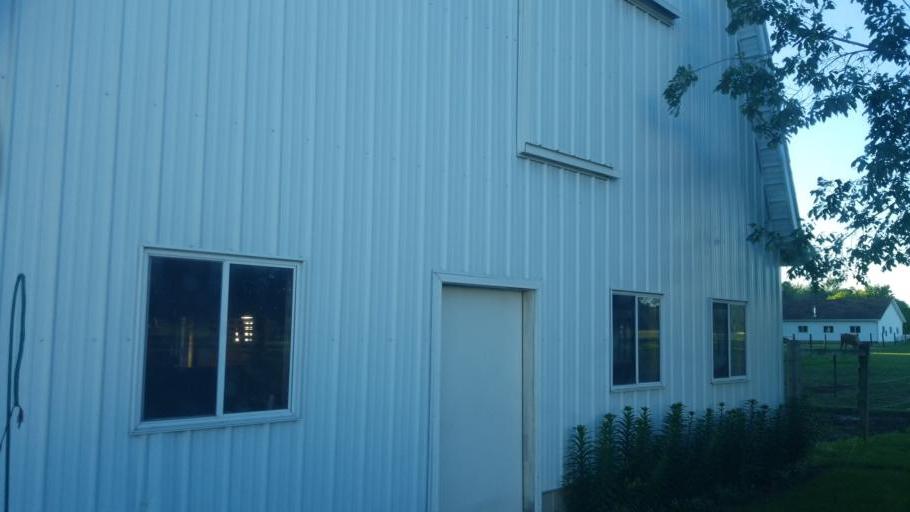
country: US
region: Indiana
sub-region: Elkhart County
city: Nappanee
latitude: 41.4307
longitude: -86.0480
